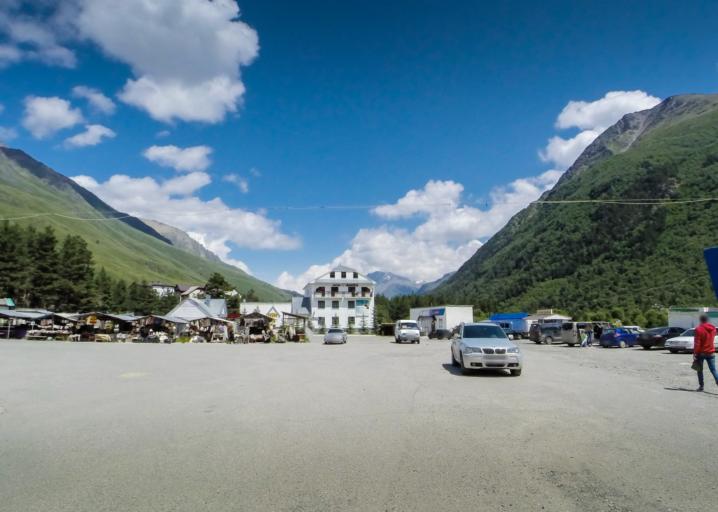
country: RU
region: Kabardino-Balkariya
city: Terskol
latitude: 43.2454
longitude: 42.5238
